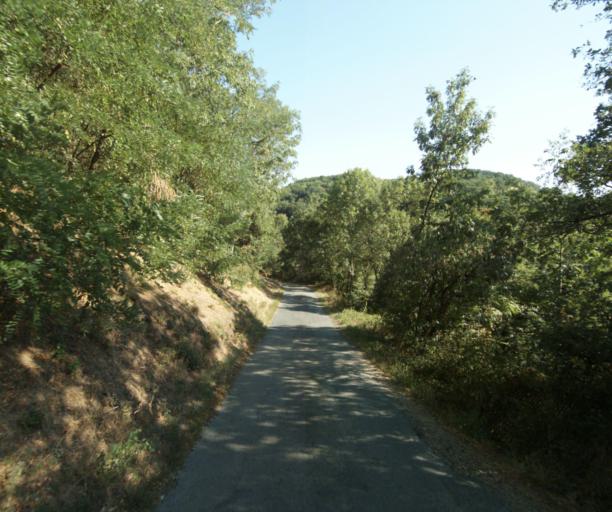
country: FR
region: Rhone-Alpes
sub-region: Departement du Rhone
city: Saint-Pierre-la-Palud
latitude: 45.7937
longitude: 4.5975
